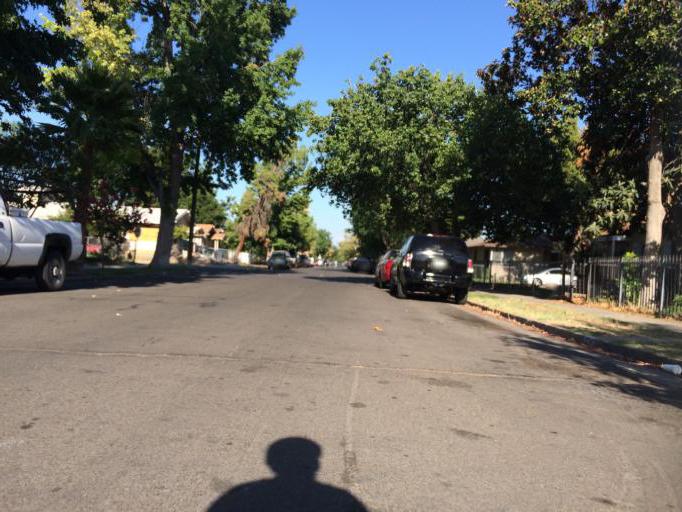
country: US
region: California
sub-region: Fresno County
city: Fresno
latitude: 36.7441
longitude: -119.7698
